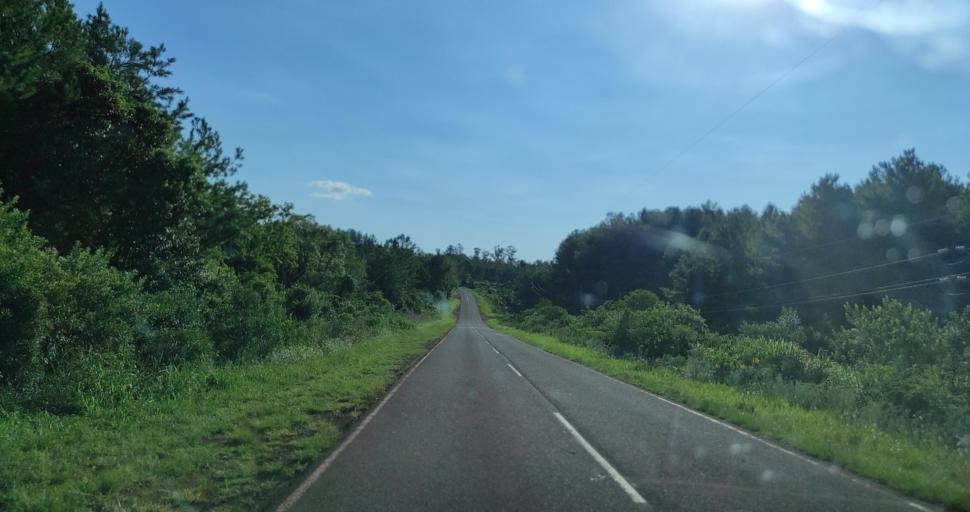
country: AR
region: Misiones
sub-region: Departamento de Eldorado
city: Eldorado
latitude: -26.3870
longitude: -54.3504
